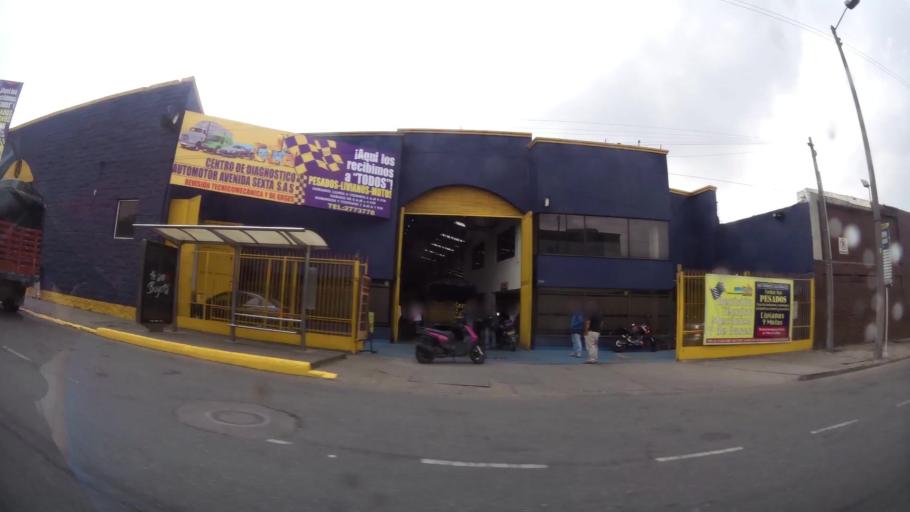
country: CO
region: Bogota D.C.
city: Bogota
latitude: 4.6177
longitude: -74.1055
